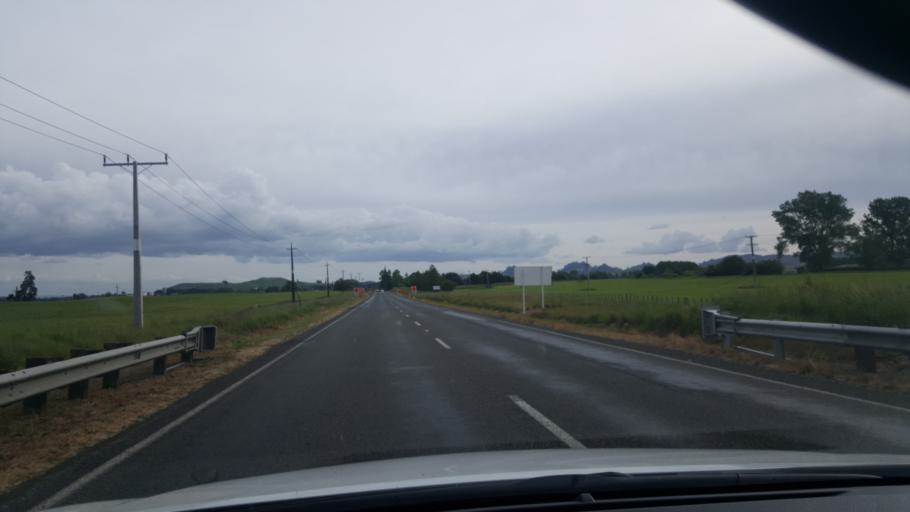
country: NZ
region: Bay of Plenty
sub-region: Rotorua District
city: Rotorua
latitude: -38.4006
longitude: 176.3315
